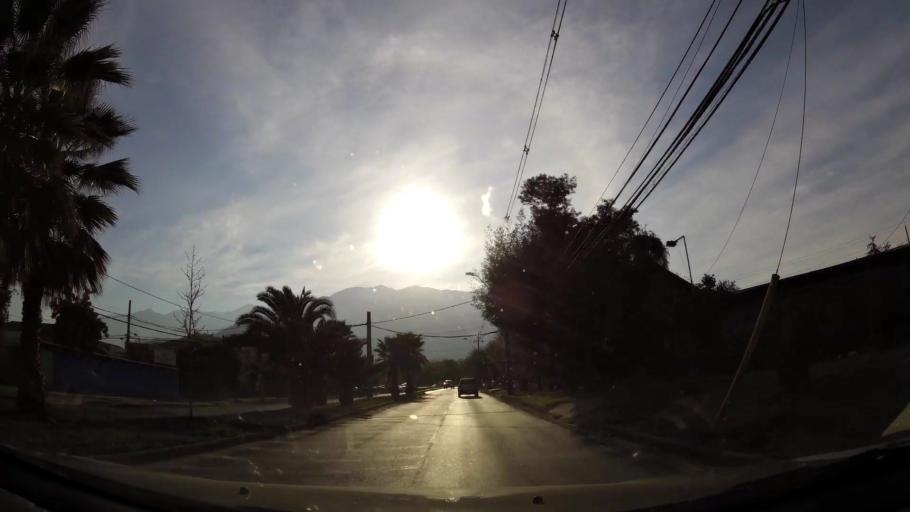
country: CL
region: Santiago Metropolitan
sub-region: Provincia de Cordillera
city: Puente Alto
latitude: -33.5589
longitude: -70.5550
